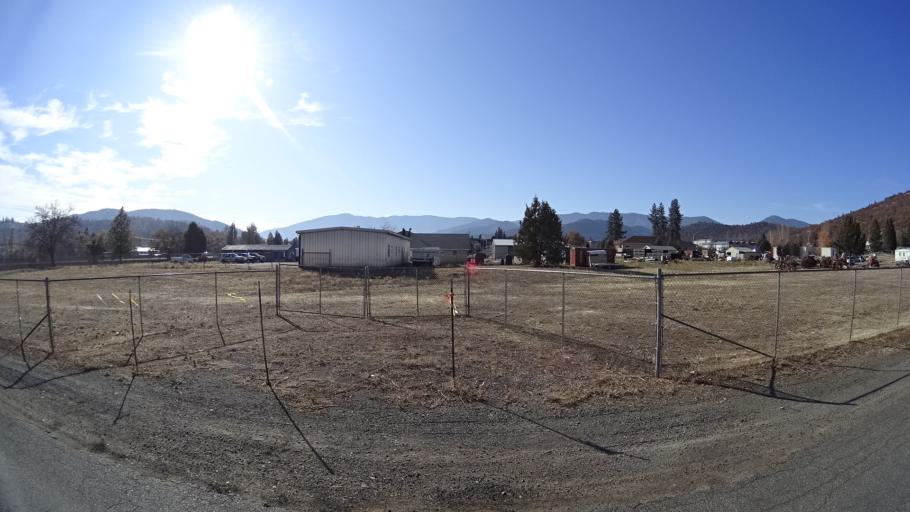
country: US
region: California
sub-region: Siskiyou County
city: Yreka
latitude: 41.7092
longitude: -122.6436
